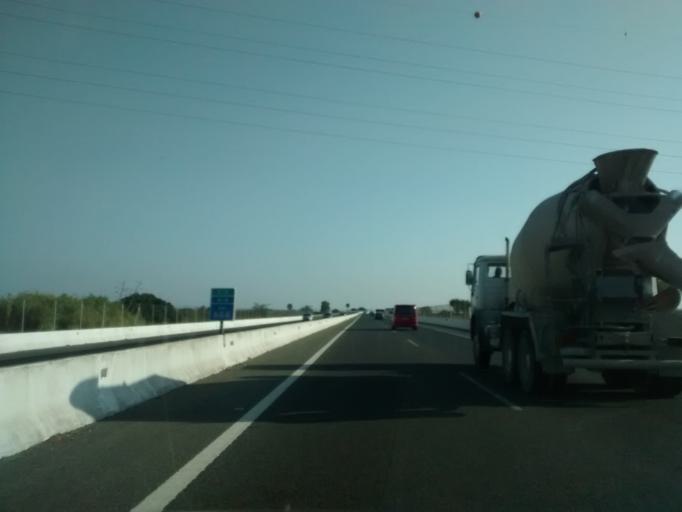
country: ES
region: Andalusia
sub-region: Provincia de Cadiz
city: San Fernando
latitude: 36.4790
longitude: -6.1448
